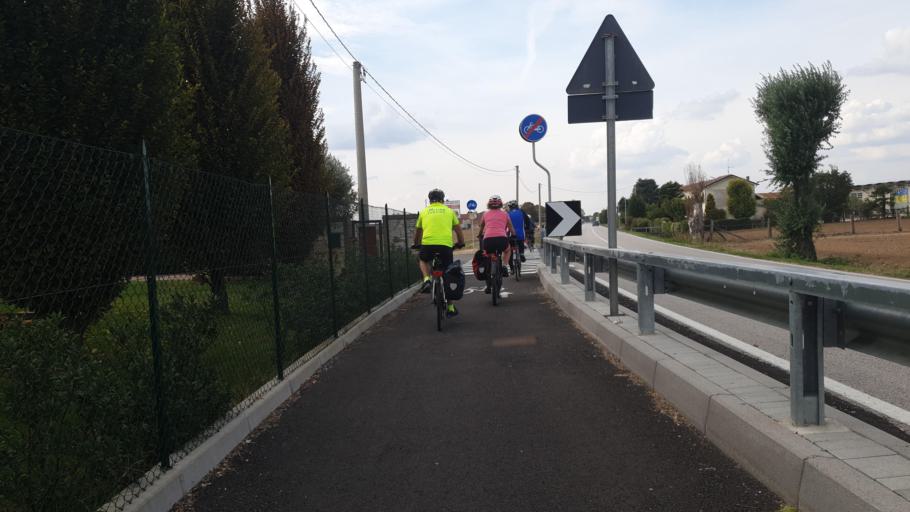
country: IT
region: Veneto
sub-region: Provincia di Vicenza
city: Poiana Maggiore
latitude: 45.2850
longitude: 11.5228
